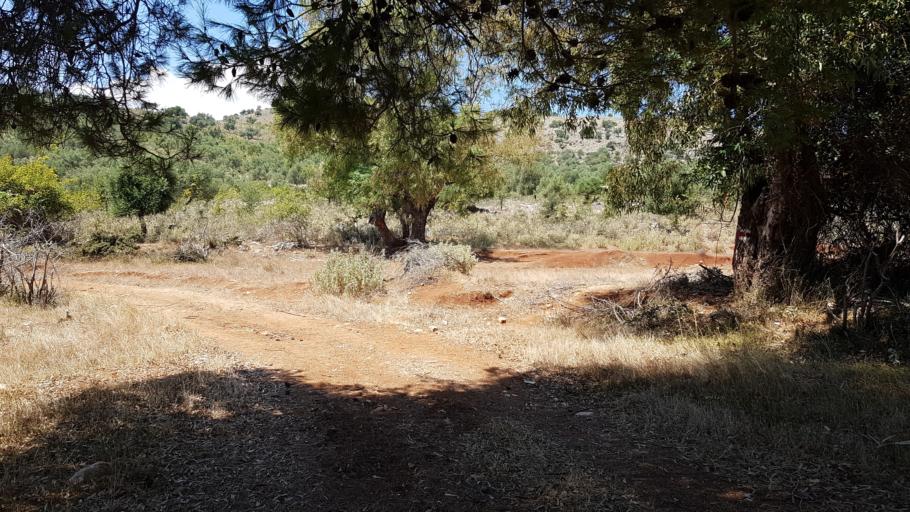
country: AL
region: Vlore
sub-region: Rrethi i Sarandes
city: Xarre
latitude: 39.7559
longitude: 19.9954
